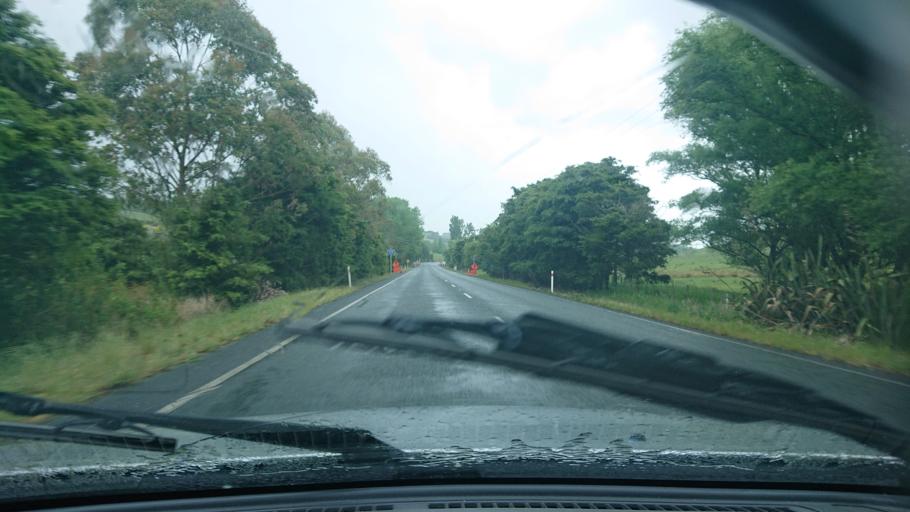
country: NZ
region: Auckland
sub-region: Auckland
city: Wellsford
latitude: -36.3175
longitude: 174.4911
